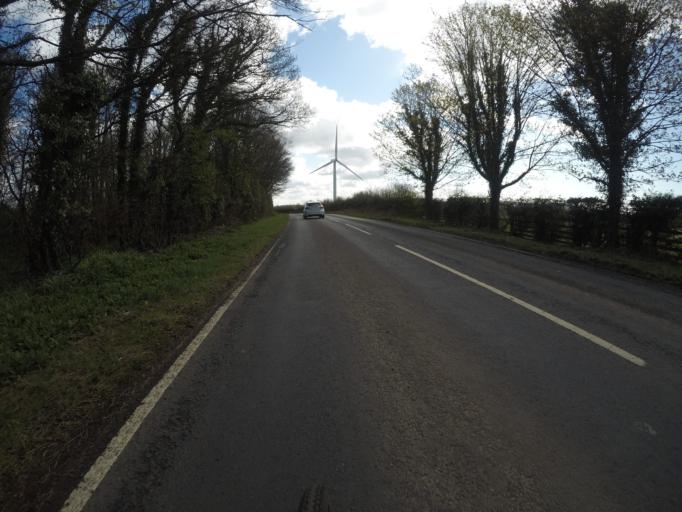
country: GB
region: Scotland
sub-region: North Ayrshire
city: Dreghorn
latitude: 55.5949
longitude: -4.6227
